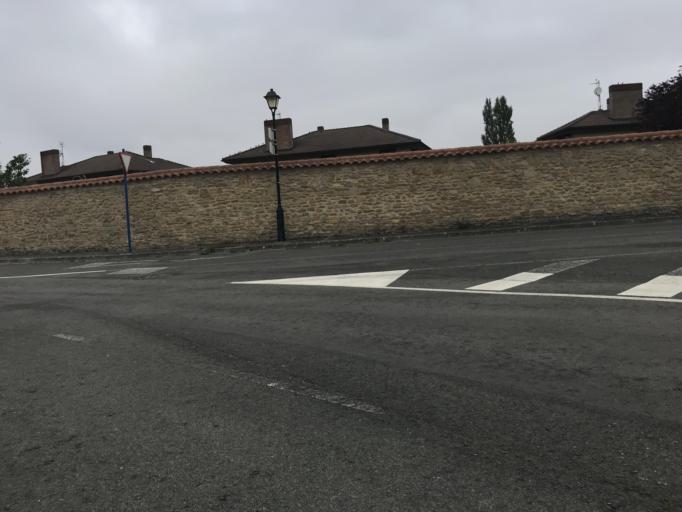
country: ES
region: Basque Country
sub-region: Provincia de Alava
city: Gasteiz / Vitoria
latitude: 42.8515
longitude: -2.6399
